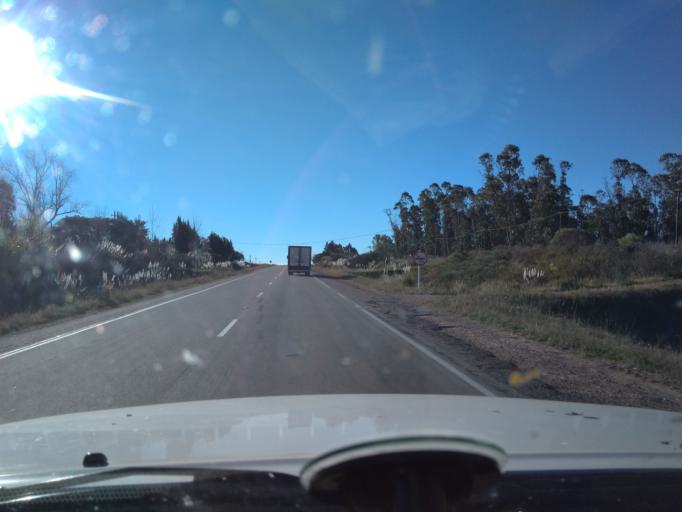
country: UY
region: Canelones
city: Sauce
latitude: -34.5925
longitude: -56.0524
